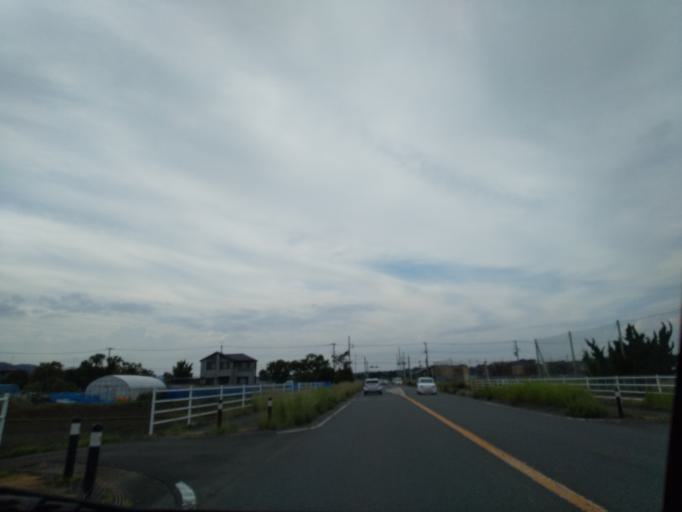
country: JP
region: Kanagawa
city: Zama
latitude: 35.4754
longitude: 139.3581
